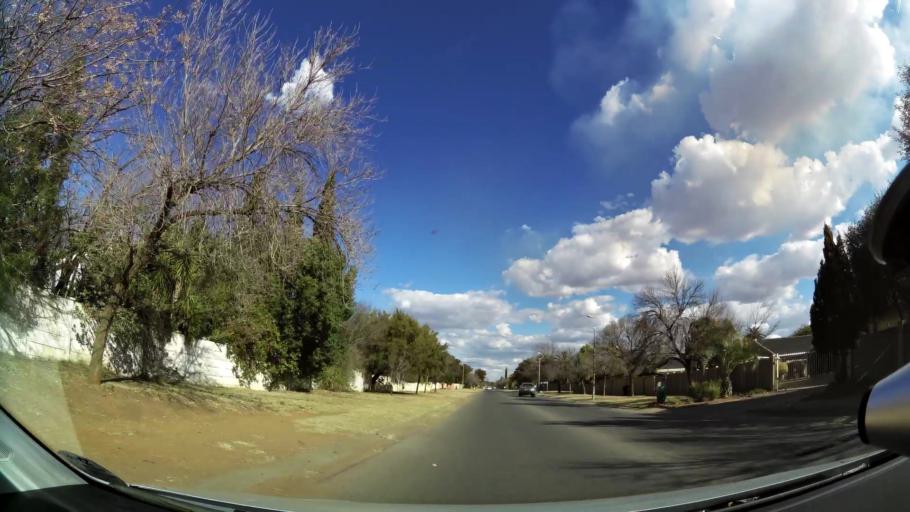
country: ZA
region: North-West
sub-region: Dr Kenneth Kaunda District Municipality
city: Klerksdorp
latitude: -26.8311
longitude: 26.6567
